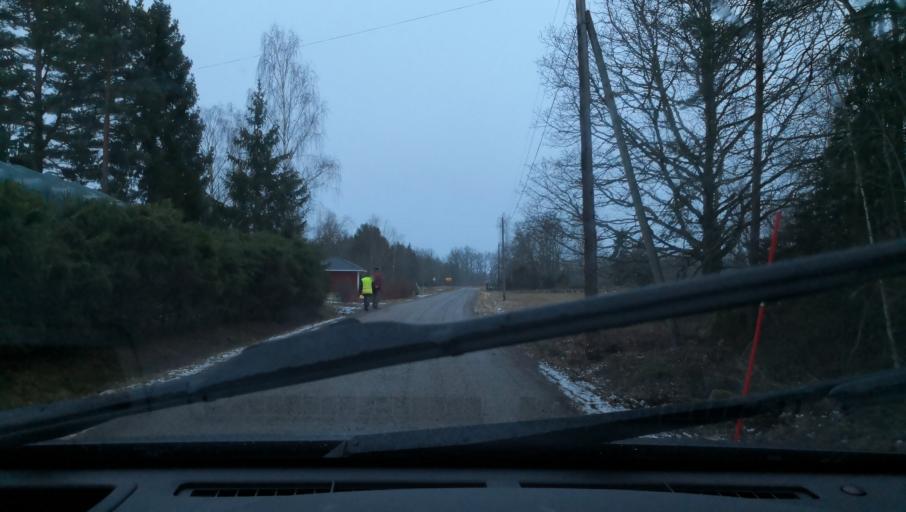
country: SE
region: Uppsala
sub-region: Enkopings Kommun
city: Hummelsta
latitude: 59.4580
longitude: 16.8262
